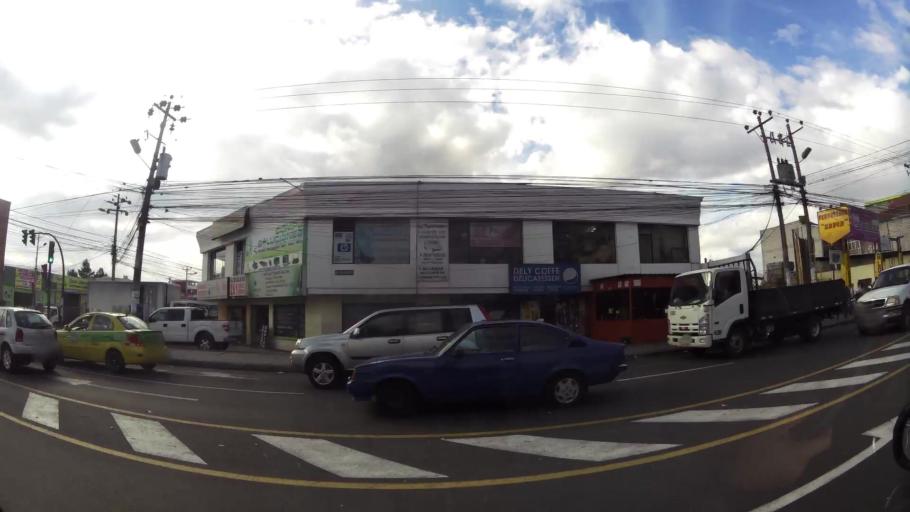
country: EC
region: Pichincha
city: Quito
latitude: -0.1287
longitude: -78.4709
